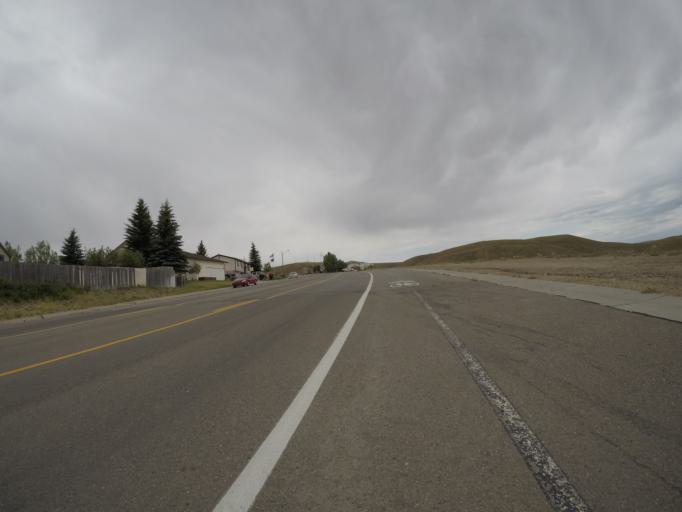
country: US
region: Wyoming
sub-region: Lincoln County
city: Kemmerer
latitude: 41.7913
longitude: -110.5506
